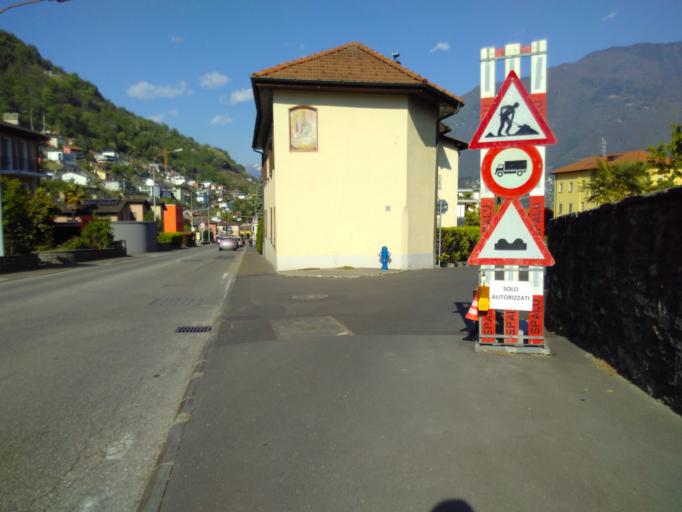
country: CH
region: Ticino
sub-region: Bellinzona District
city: Monte Carasso
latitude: 46.1871
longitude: 8.9945
